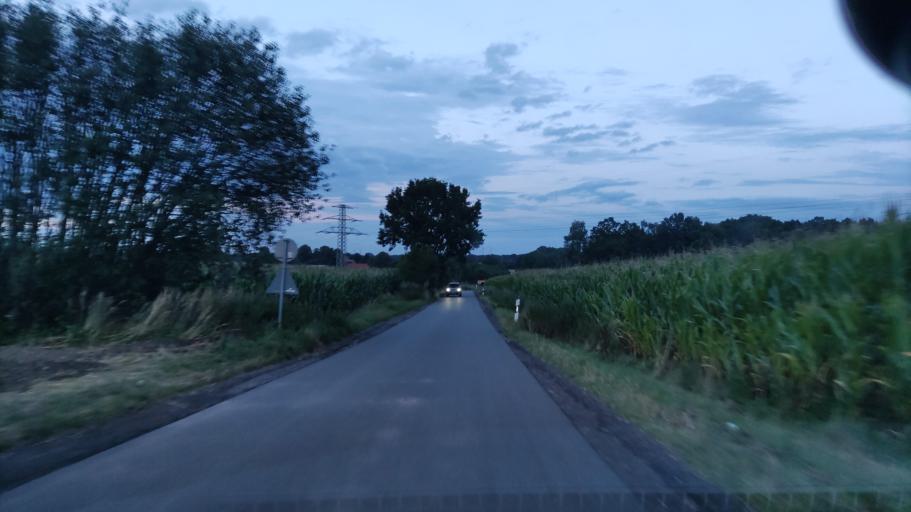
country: DE
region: Schleswig-Holstein
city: Kruzen
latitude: 53.3950
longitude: 10.5214
